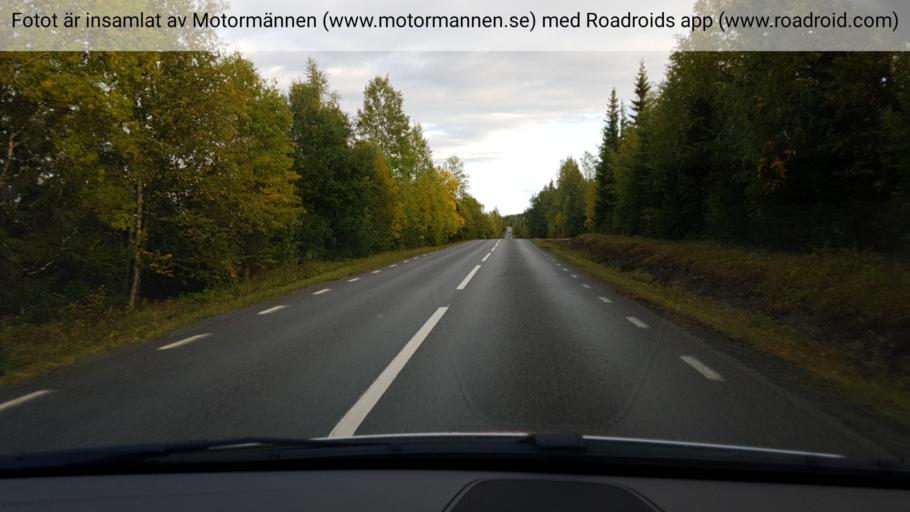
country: SE
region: Jaemtland
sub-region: Krokoms Kommun
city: Krokom
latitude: 63.1594
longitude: 14.1351
